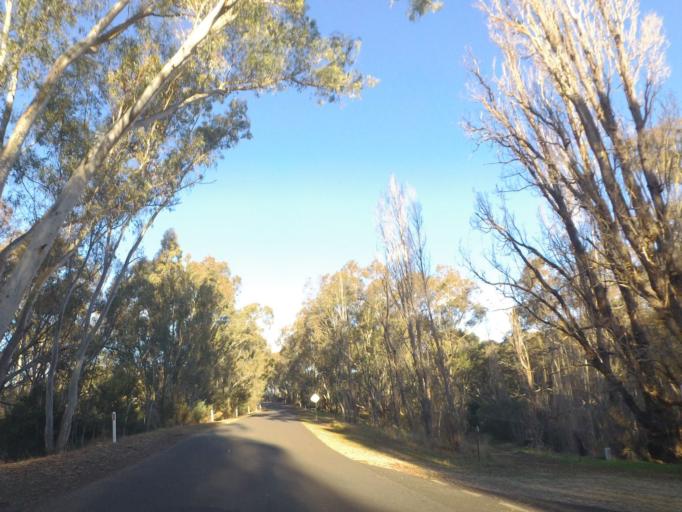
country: AU
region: Victoria
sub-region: Mount Alexander
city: Castlemaine
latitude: -37.1573
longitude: 144.2104
